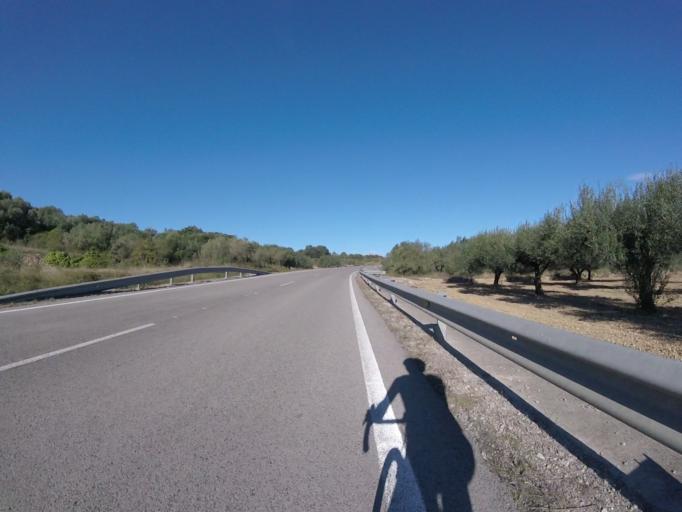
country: ES
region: Valencia
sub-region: Provincia de Castello
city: Cervera del Maestre
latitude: 40.4703
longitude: 0.2430
